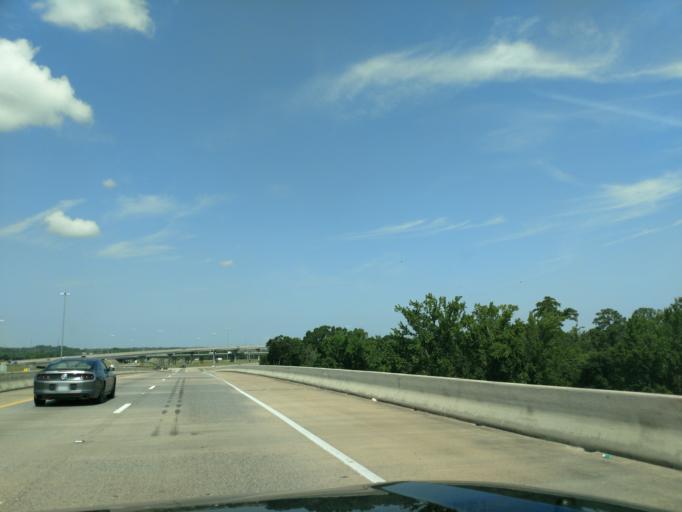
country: US
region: Mississippi
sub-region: Hinds County
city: Jackson
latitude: 32.2756
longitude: -90.1669
